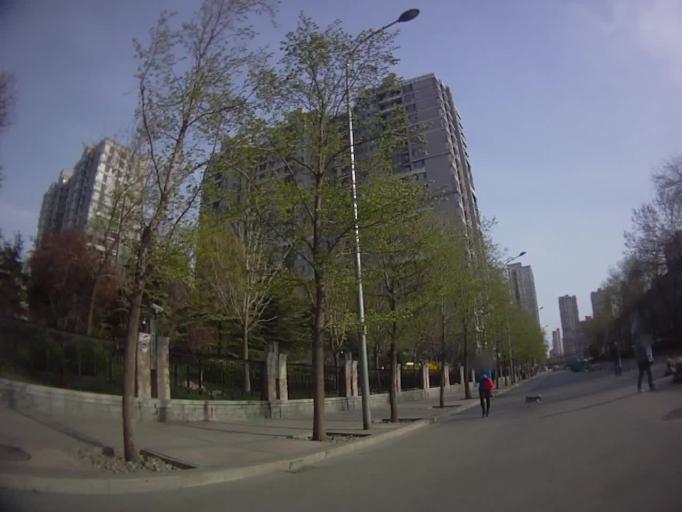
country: CN
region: Beijing
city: Longtan
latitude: 39.8944
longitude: 116.4442
